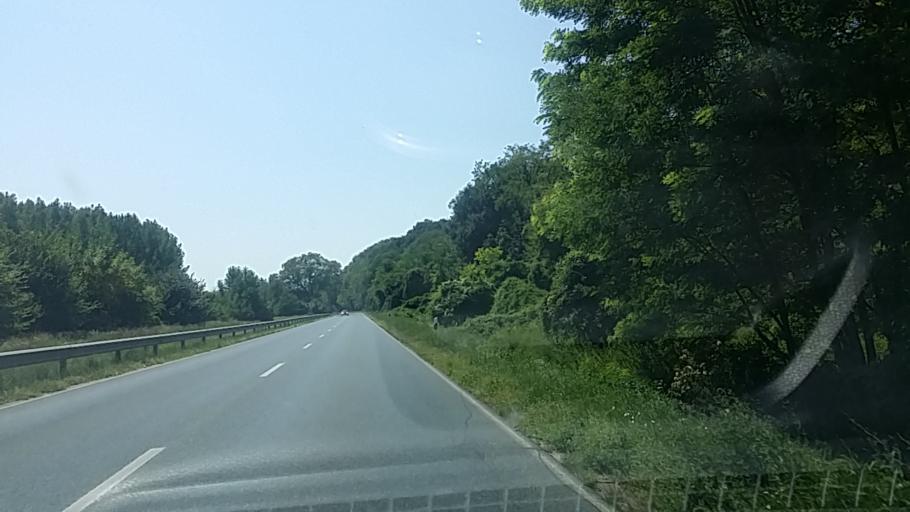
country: HU
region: Tolna
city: Paks
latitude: 46.6470
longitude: 18.8808
